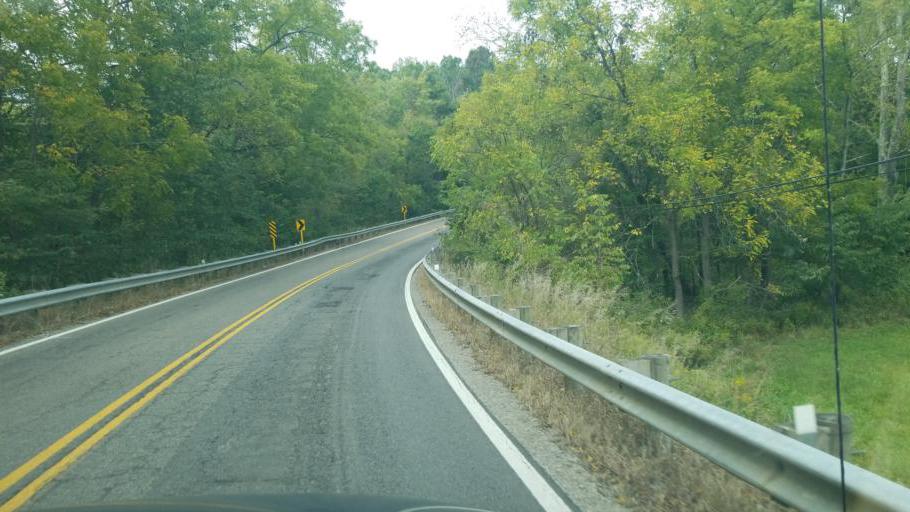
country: US
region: Ohio
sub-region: Licking County
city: Newark
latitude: 40.0040
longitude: -82.2887
